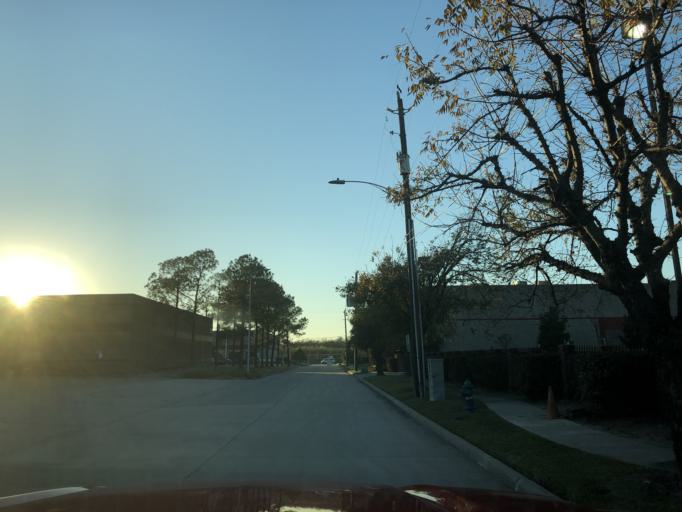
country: US
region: Texas
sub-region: Harris County
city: Jacinto City
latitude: 29.7586
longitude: -95.2663
